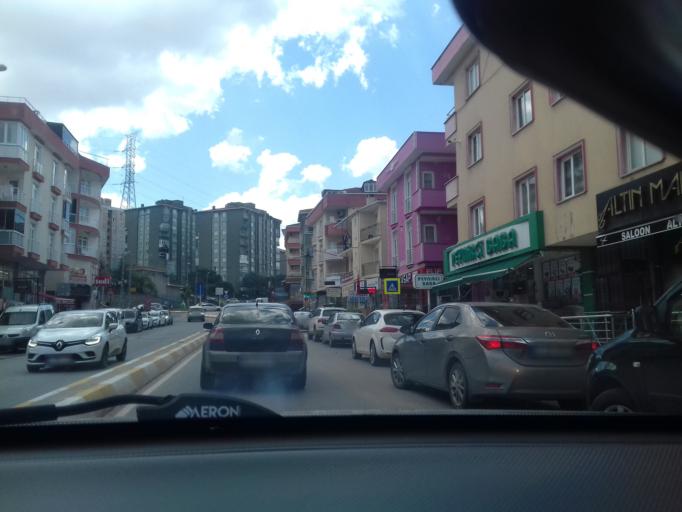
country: TR
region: Istanbul
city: Pendik
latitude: 40.9162
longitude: 29.2855
